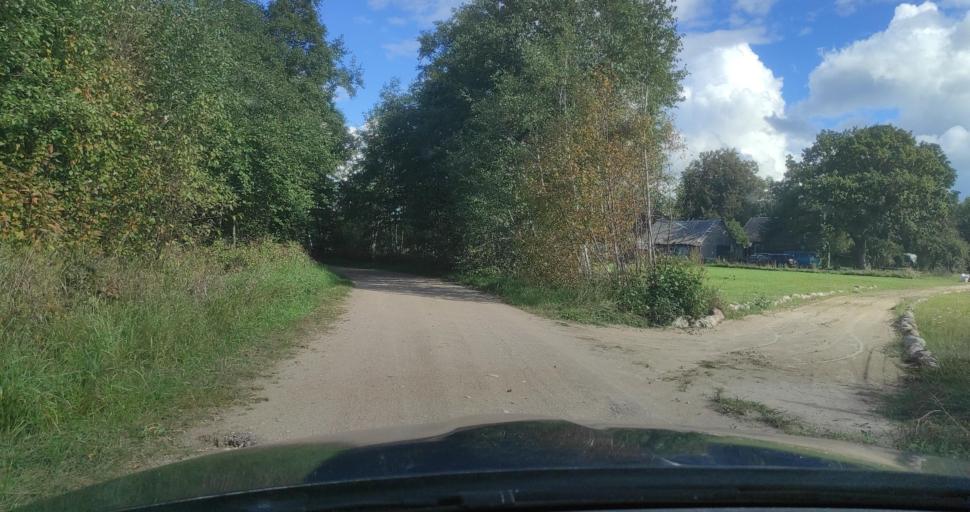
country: LV
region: Ventspils
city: Ventspils
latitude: 57.3682
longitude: 21.6312
